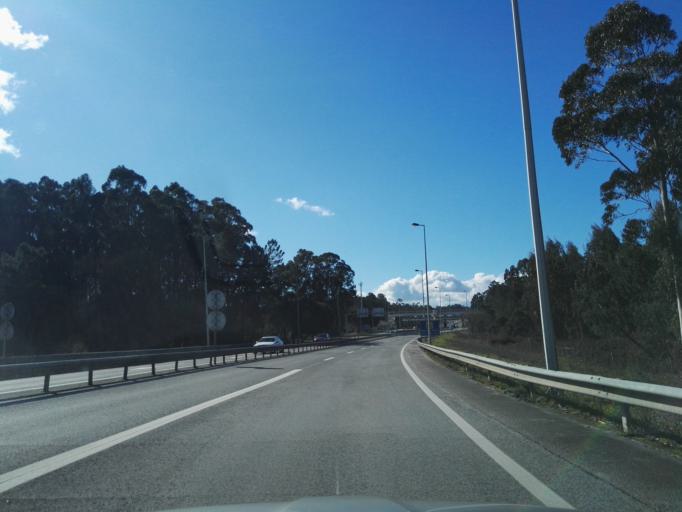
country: PT
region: Santarem
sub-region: Ourem
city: Fatima
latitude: 39.6295
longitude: -8.6844
